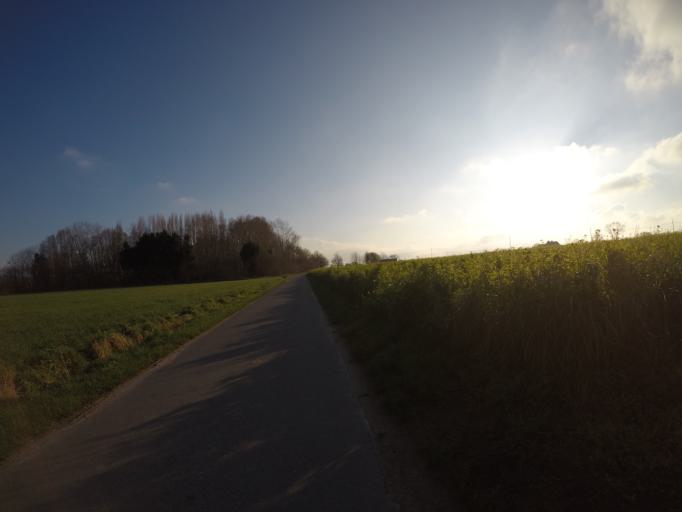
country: BE
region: Flanders
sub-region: Provincie West-Vlaanderen
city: Lichtervelde
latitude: 51.0524
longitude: 3.1920
